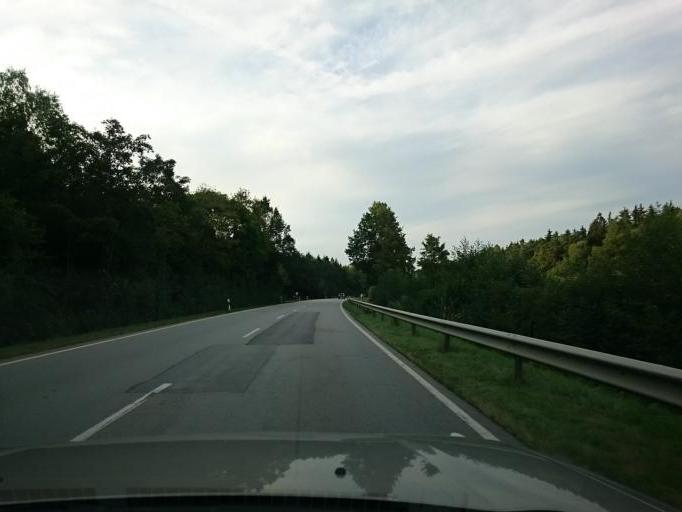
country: DE
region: Bavaria
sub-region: Lower Bavaria
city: Simbach
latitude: 48.5773
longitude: 12.7248
